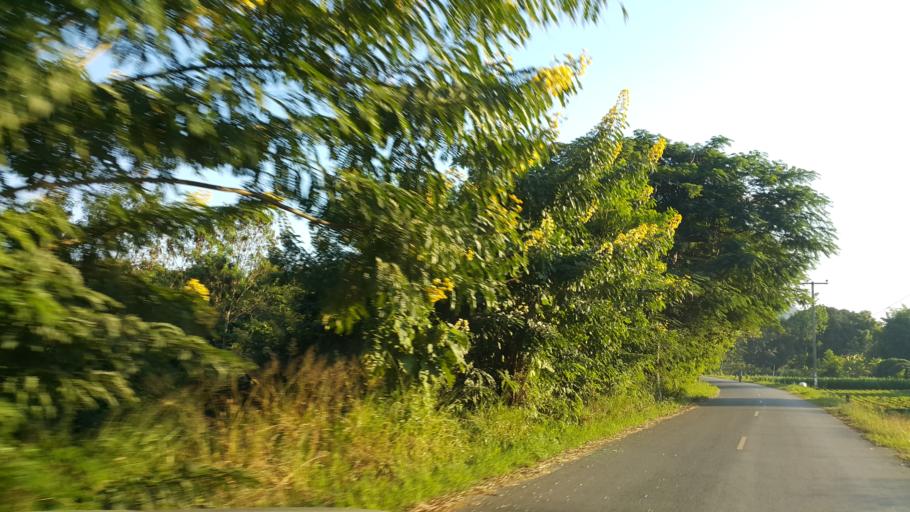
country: TH
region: Chiang Mai
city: Mae On
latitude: 18.7543
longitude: 99.2433
